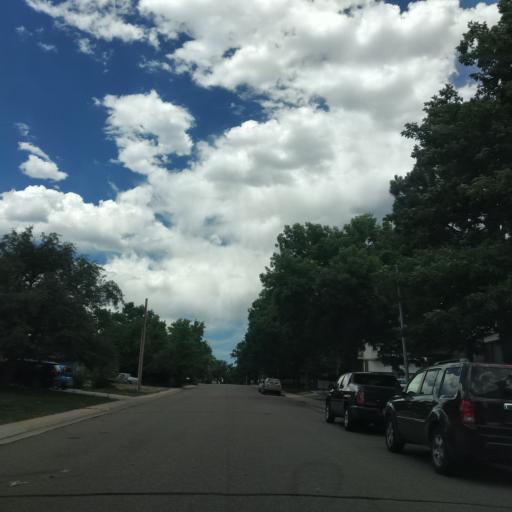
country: US
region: Colorado
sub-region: Jefferson County
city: Lakewood
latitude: 39.6837
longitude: -105.0873
